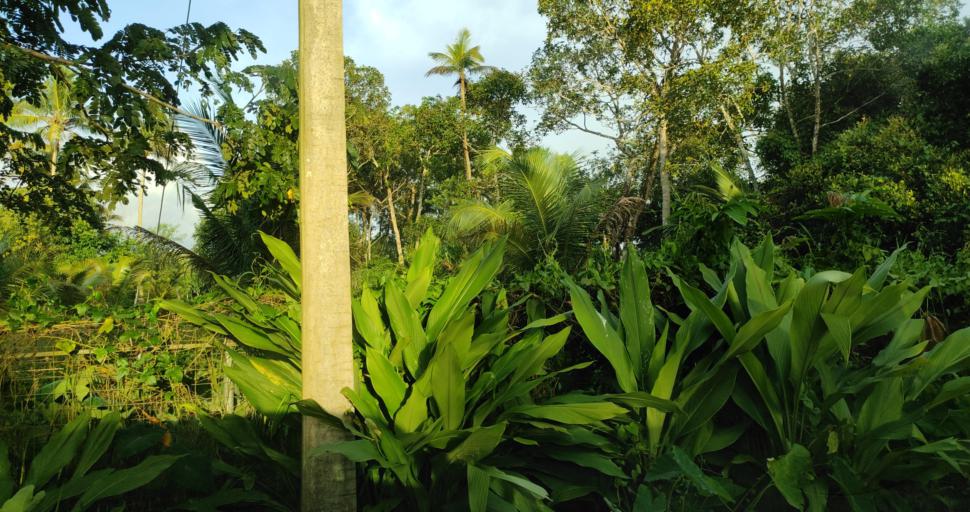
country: IN
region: Kerala
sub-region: Alappuzha
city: Shertallai
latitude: 9.6150
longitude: 76.3330
